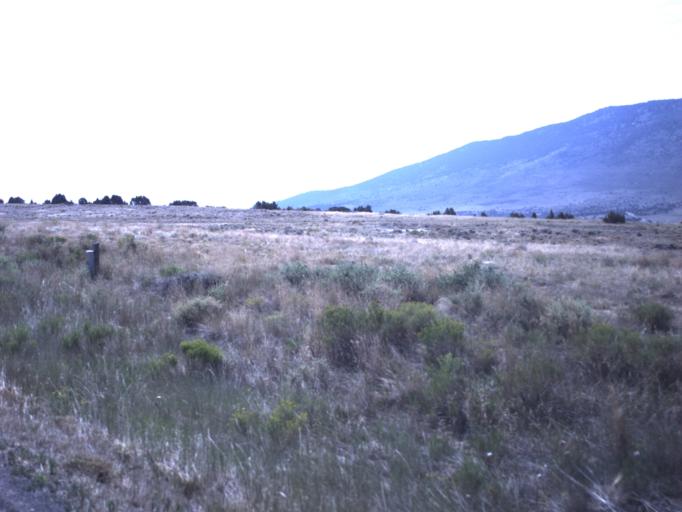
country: US
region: Utah
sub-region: Daggett County
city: Manila
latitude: 40.9785
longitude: -109.8040
